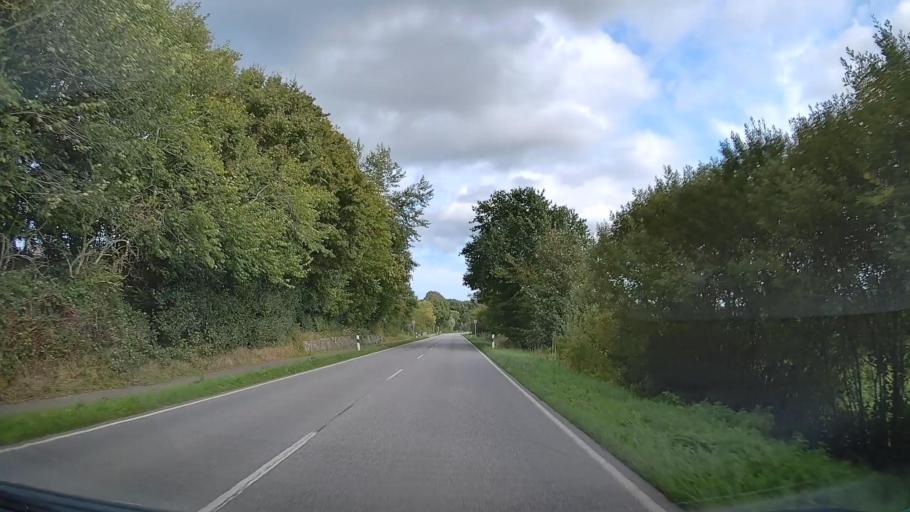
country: DE
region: Schleswig-Holstein
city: Niesgrau
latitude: 54.7506
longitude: 9.8430
